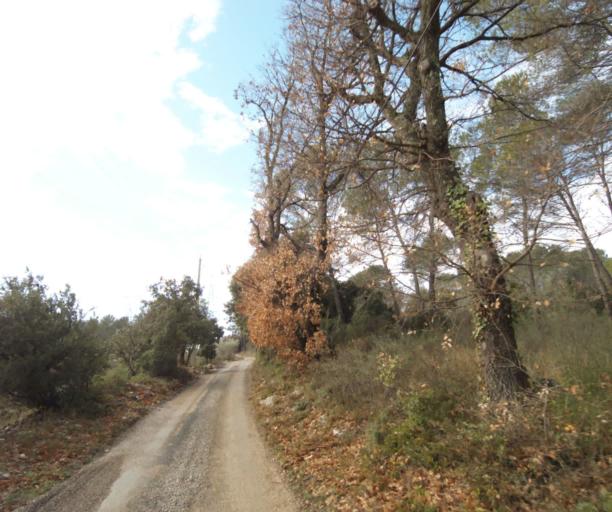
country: FR
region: Provence-Alpes-Cote d'Azur
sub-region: Departement du Var
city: Trans-en-Provence
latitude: 43.4998
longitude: 6.4677
